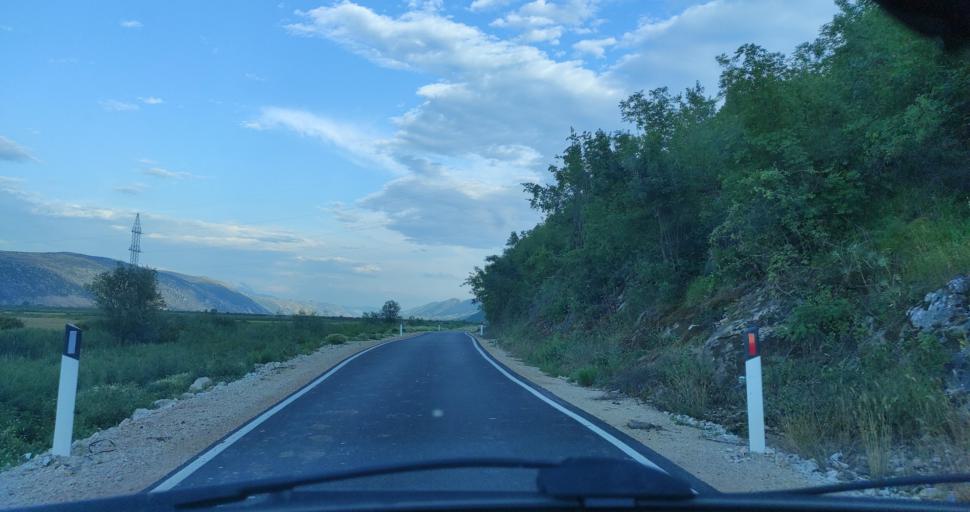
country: AL
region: Shkoder
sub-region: Rrethi i Shkodres
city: Velipoje
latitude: 41.9278
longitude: 19.4464
